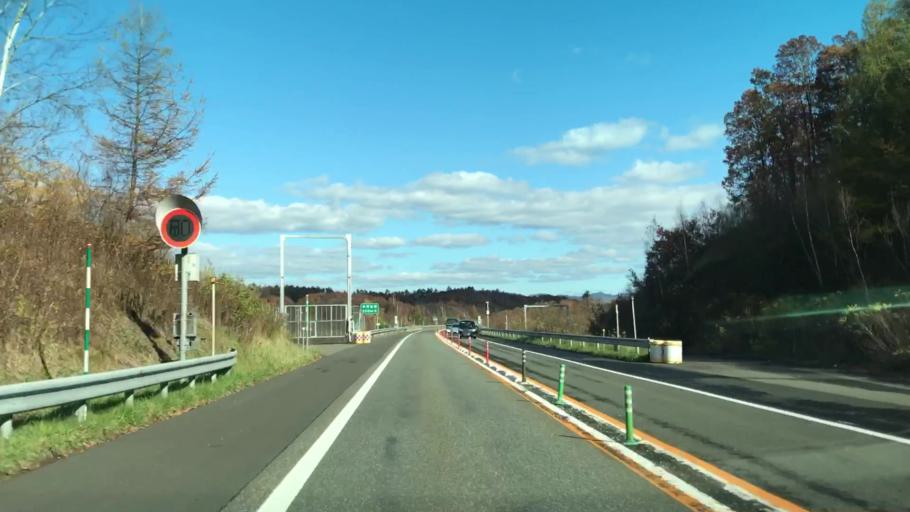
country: JP
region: Hokkaido
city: Chitose
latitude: 42.8964
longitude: 141.8356
